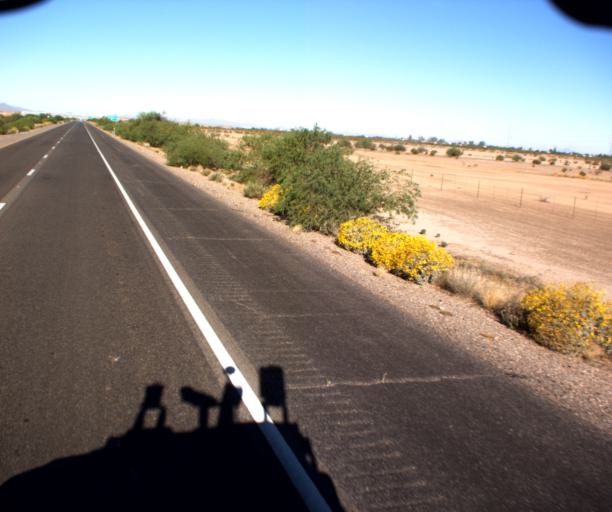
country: US
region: Arizona
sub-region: Pinal County
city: Casa Grande
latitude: 32.8282
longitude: -111.8529
